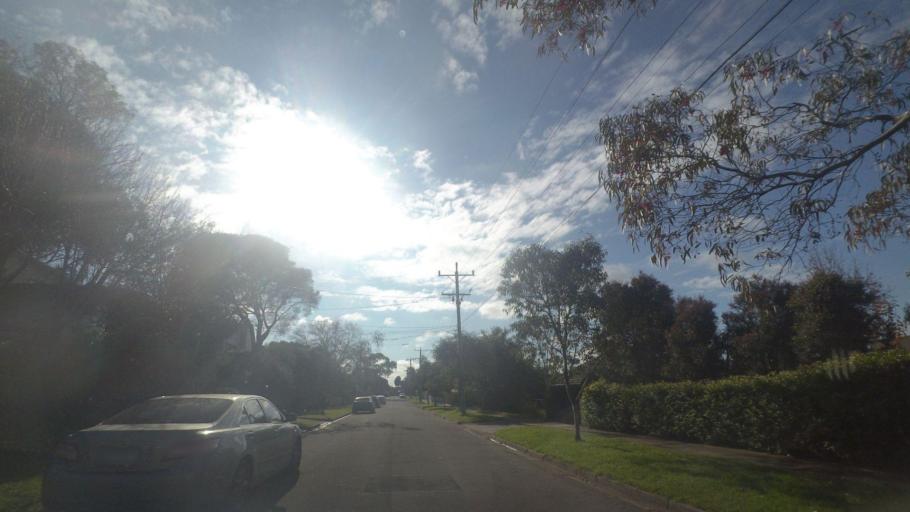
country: AU
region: Victoria
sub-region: Whitehorse
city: Mont Albert North
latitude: -37.7977
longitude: 145.1081
